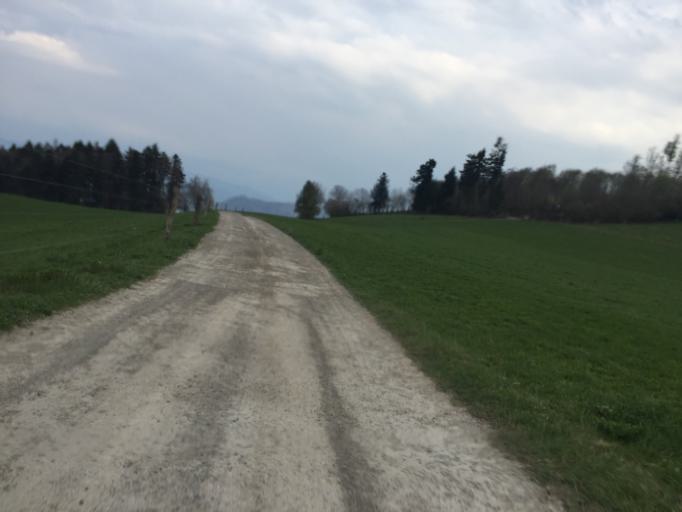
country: CH
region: Bern
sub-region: Bern-Mittelland District
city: Kehrsatz
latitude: 46.9176
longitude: 7.4496
